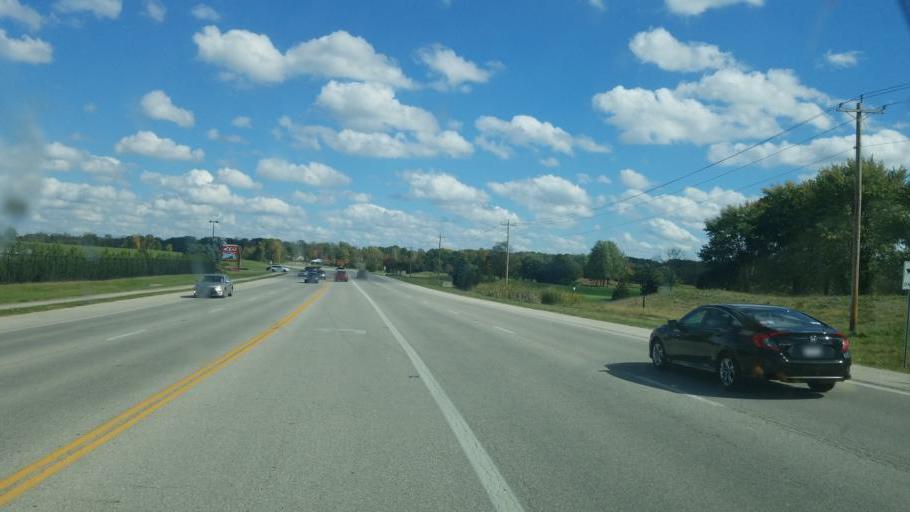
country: US
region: Ohio
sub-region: Delaware County
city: Powell
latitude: 40.1519
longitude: -83.1189
